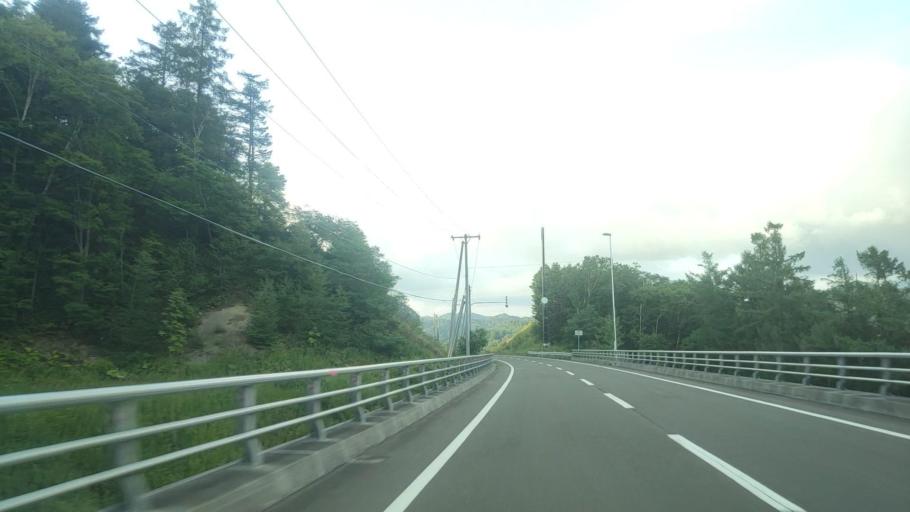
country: JP
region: Hokkaido
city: Bibai
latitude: 43.0677
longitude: 142.1033
